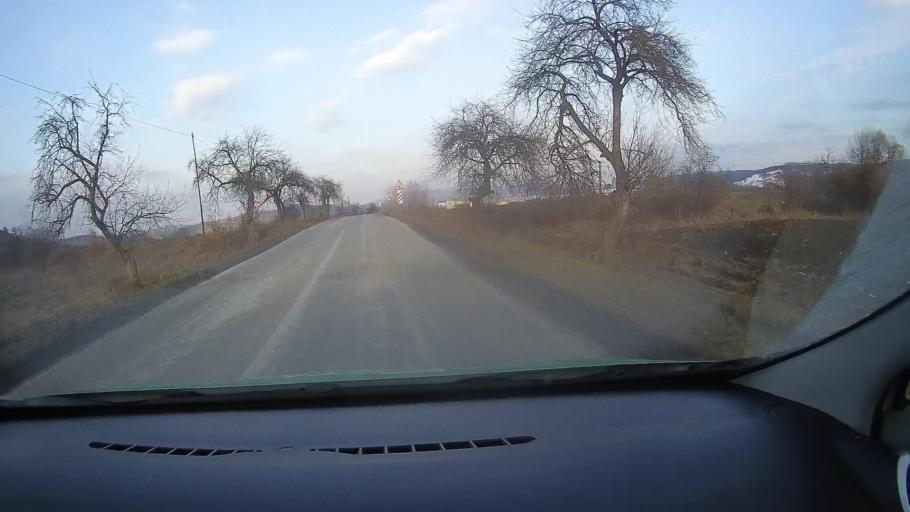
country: RO
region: Harghita
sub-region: Oras Cristuru Secuiesc
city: Filias
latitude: 46.2791
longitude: 25.0045
